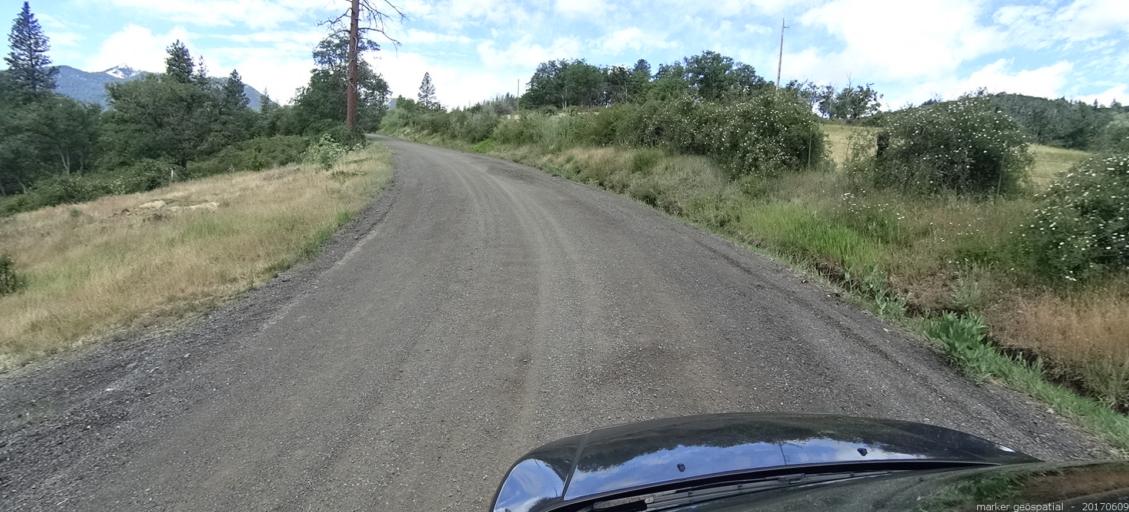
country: US
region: California
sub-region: Siskiyou County
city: Weed
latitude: 41.3108
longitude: -122.8290
